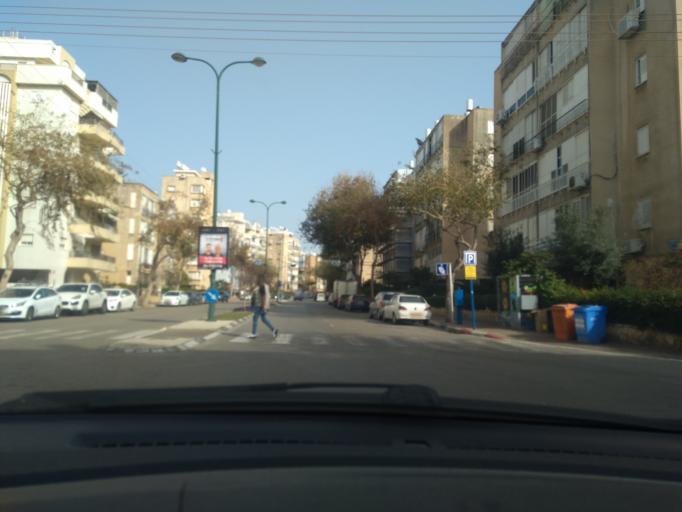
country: IL
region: Central District
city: Netanya
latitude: 32.3317
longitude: 34.8601
